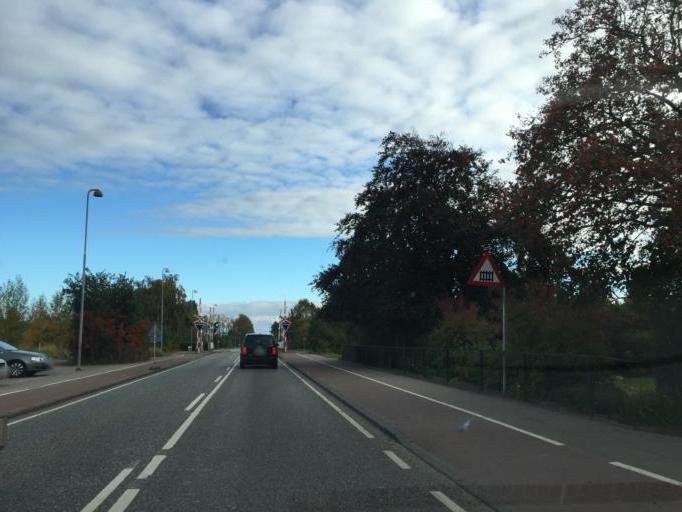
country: DK
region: Zealand
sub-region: Odsherred Kommune
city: Horve
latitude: 55.7857
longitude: 11.4680
